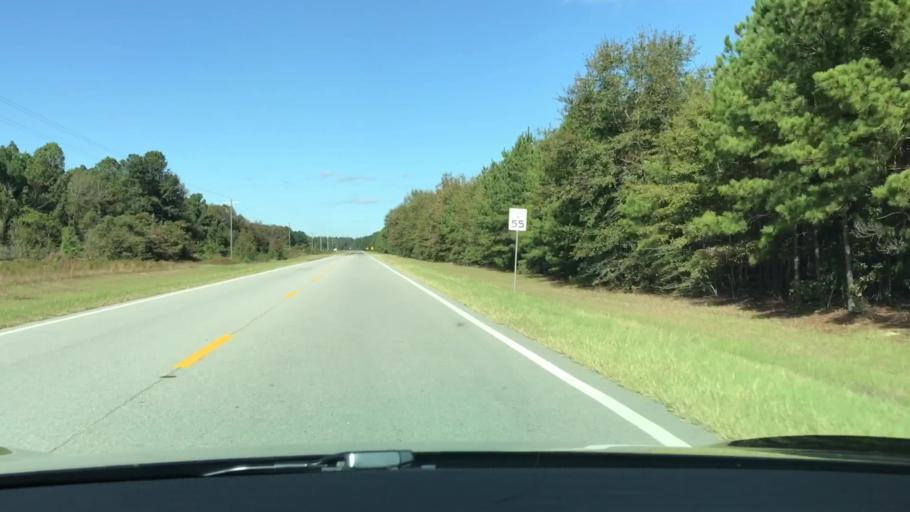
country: US
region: Georgia
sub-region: Glascock County
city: Gibson
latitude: 33.2991
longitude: -82.5172
